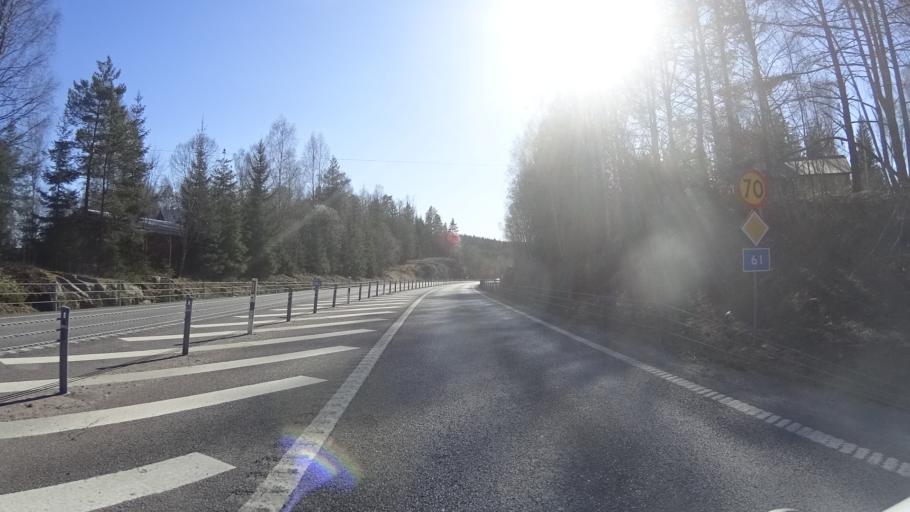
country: SE
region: Vaermland
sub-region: Arvika Kommun
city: Arvika
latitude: 59.6473
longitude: 12.7476
